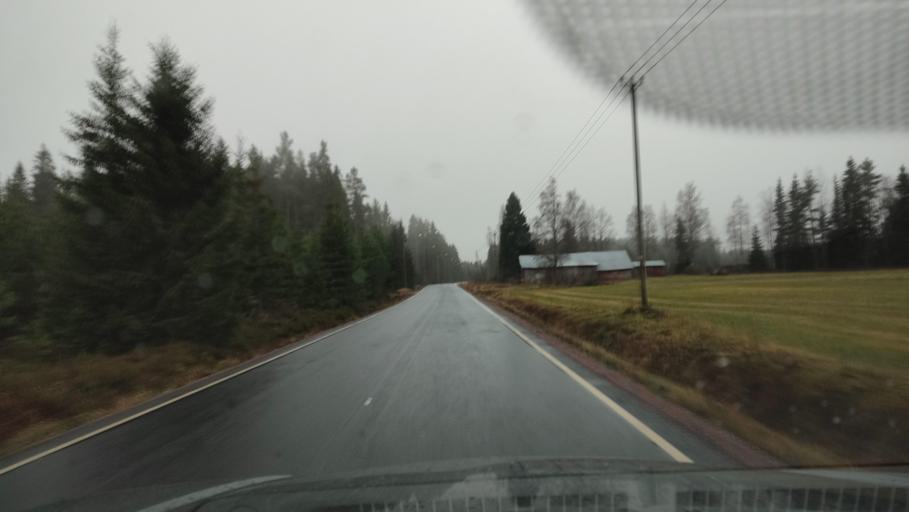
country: FI
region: Southern Ostrobothnia
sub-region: Suupohja
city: Karijoki
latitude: 62.1487
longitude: 21.6999
